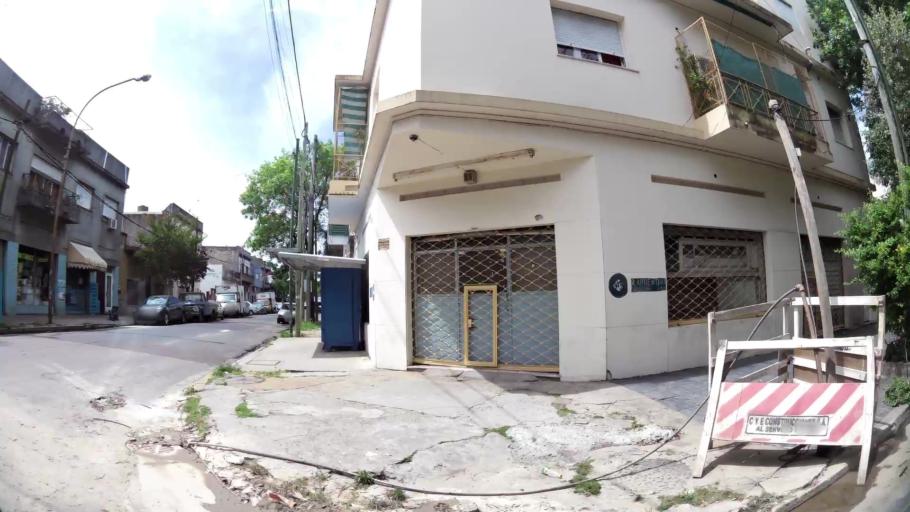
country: AR
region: Buenos Aires
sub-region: Partido de Lanus
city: Lanus
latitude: -34.6674
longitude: -58.4077
